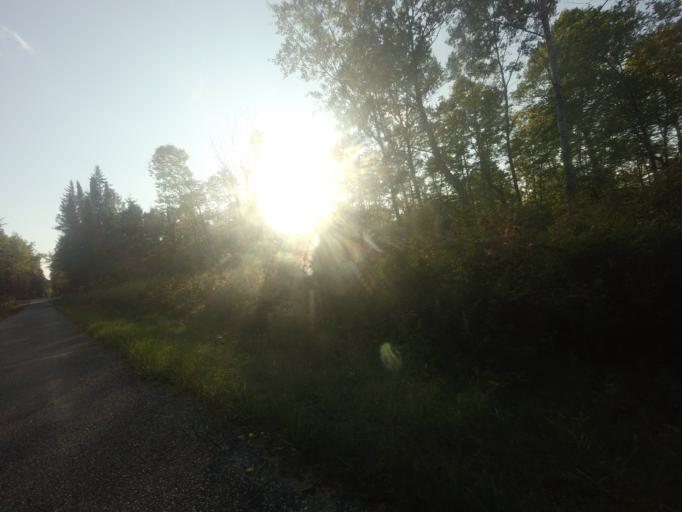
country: CA
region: Quebec
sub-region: Laurentides
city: Riviere-Rouge
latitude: 46.4023
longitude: -74.9818
